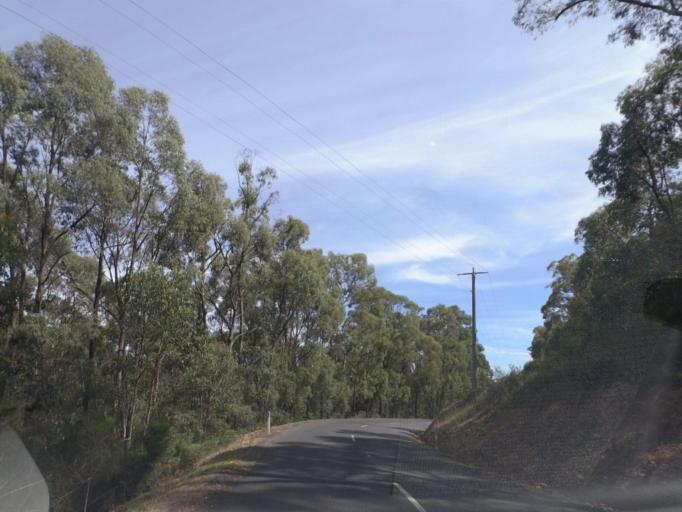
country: AU
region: Victoria
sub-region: Nillumbik
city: Saint Andrews
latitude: -37.5037
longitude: 145.3775
